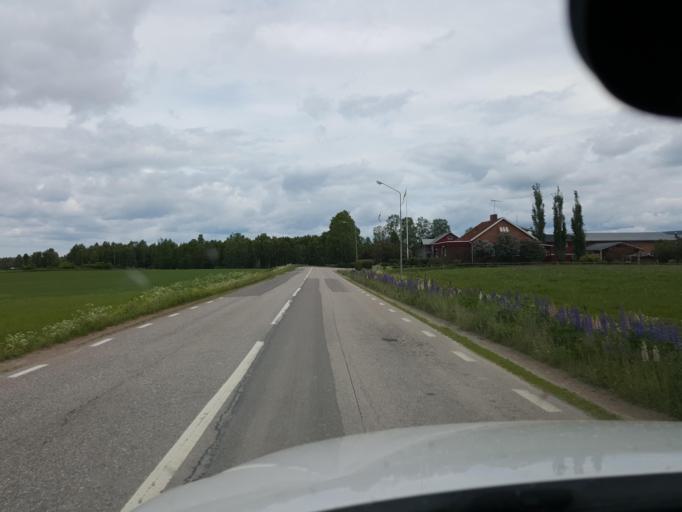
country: SE
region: Gaevleborg
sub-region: Ljusdals Kommun
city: Farila
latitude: 61.8095
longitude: 15.7397
